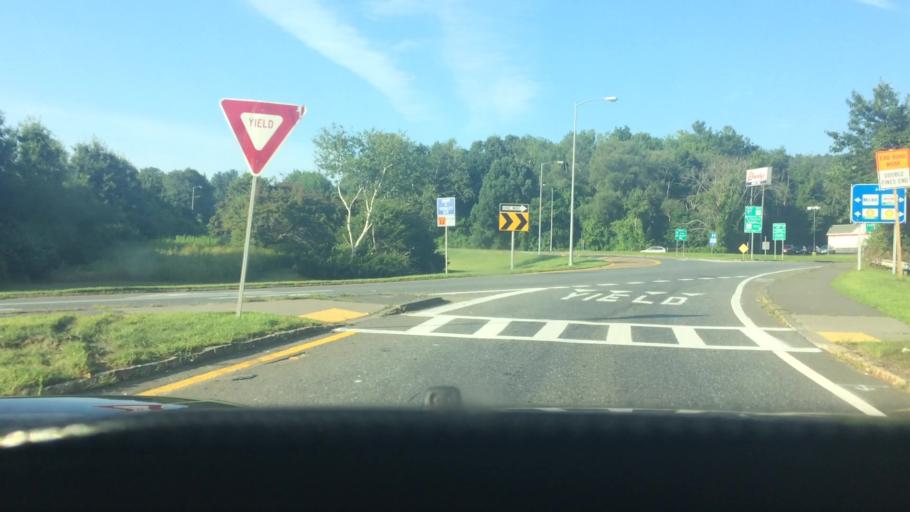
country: US
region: Massachusetts
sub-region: Franklin County
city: Greenfield
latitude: 42.5863
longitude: -72.6219
